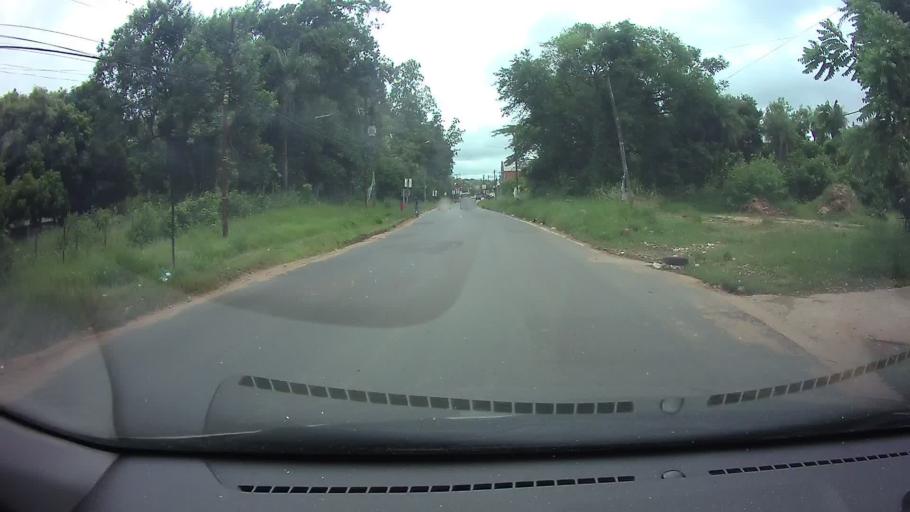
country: PY
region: Central
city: Nemby
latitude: -25.3809
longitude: -57.5468
